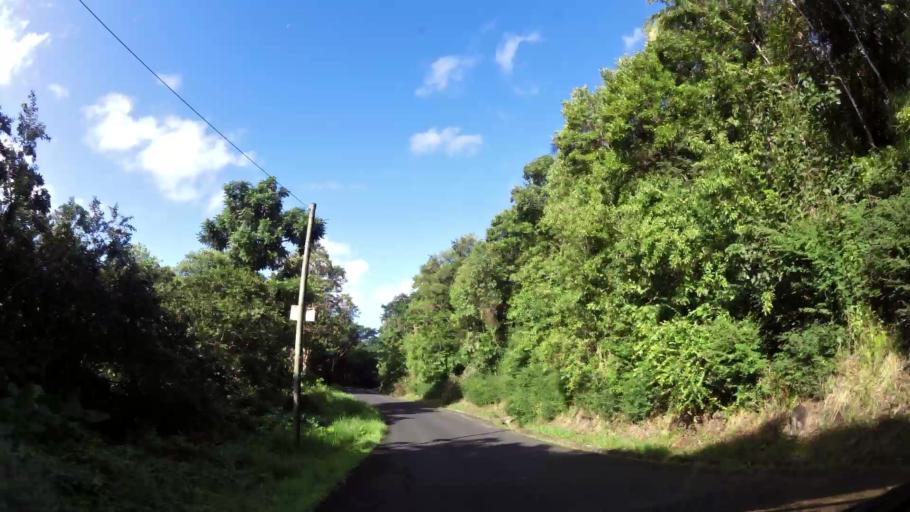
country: DM
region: Saint John
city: Portsmouth
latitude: 15.5741
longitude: -61.4408
